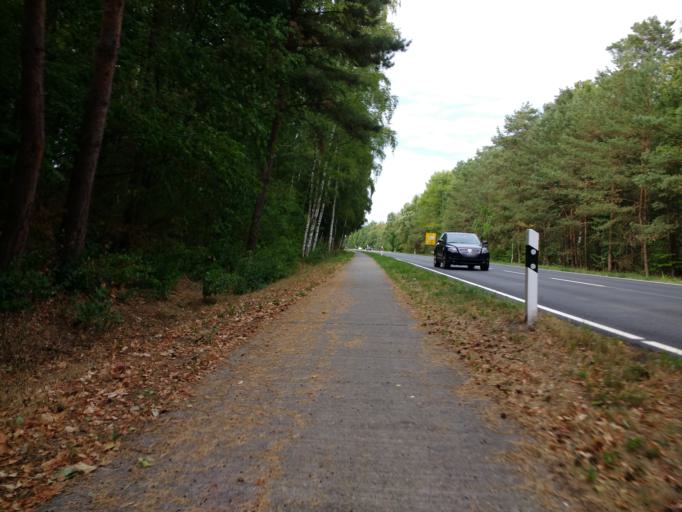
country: DE
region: Lower Saxony
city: Gifhorn
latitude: 52.4709
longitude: 10.5767
